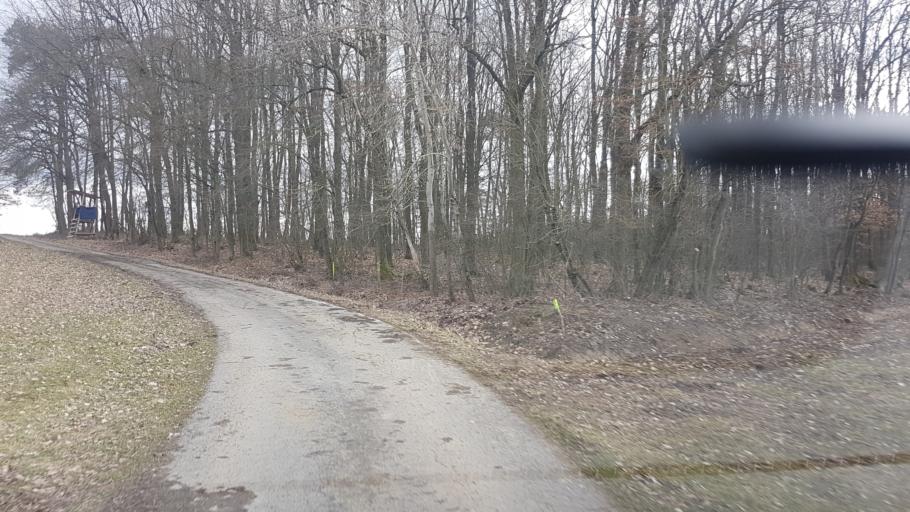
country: DE
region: Bavaria
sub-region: Upper Franconia
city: Hirschaid
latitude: 49.7910
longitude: 10.9718
